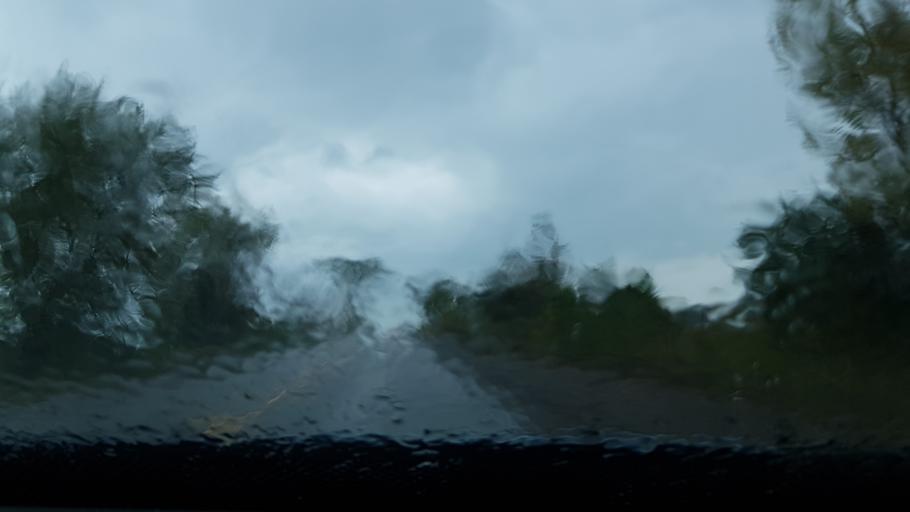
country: CA
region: Ontario
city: Omemee
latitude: 44.3935
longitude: -78.5605
